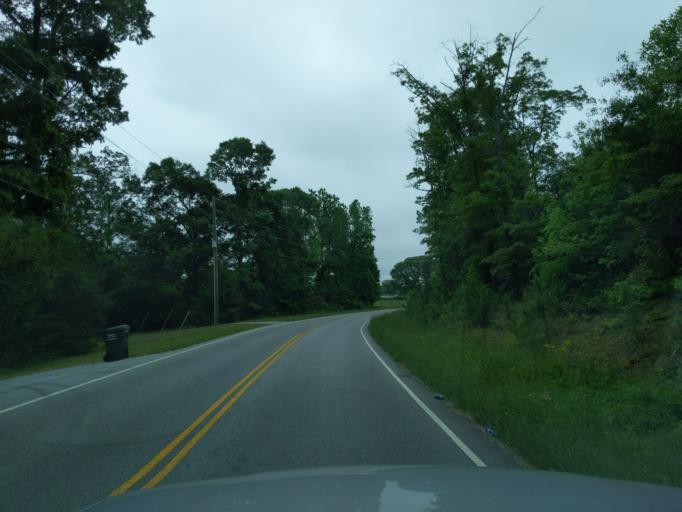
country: US
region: South Carolina
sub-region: Greenville County
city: Five Forks
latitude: 34.8571
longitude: -82.2046
